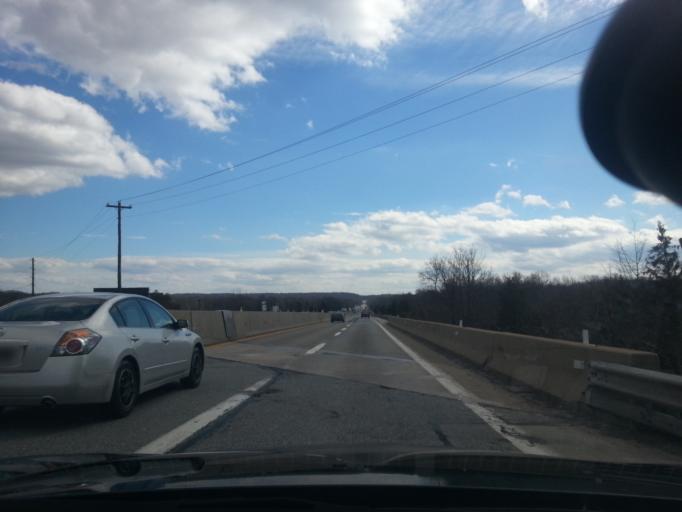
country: US
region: Pennsylvania
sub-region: Bucks County
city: Spinnerstown
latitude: 40.4183
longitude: -75.4150
